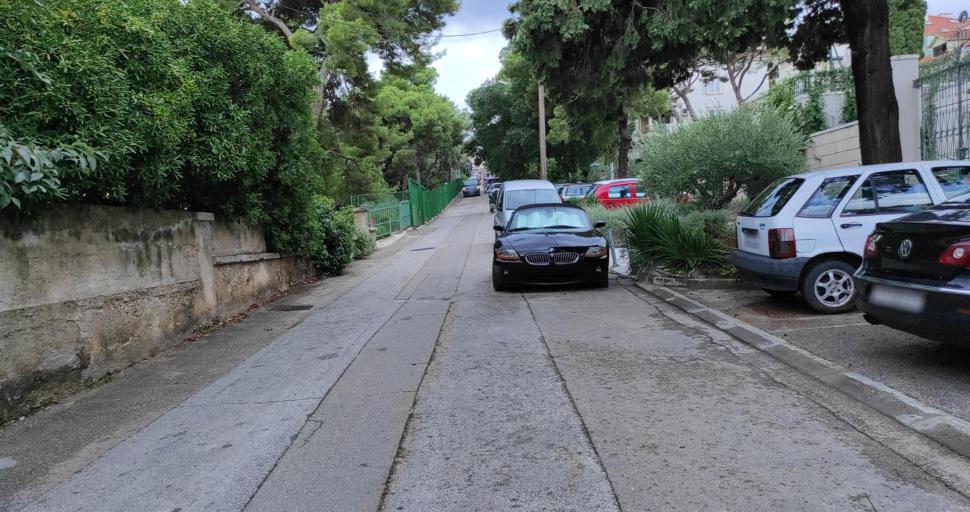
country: HR
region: Splitsko-Dalmatinska
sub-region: Grad Split
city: Split
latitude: 43.5096
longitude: 16.4310
